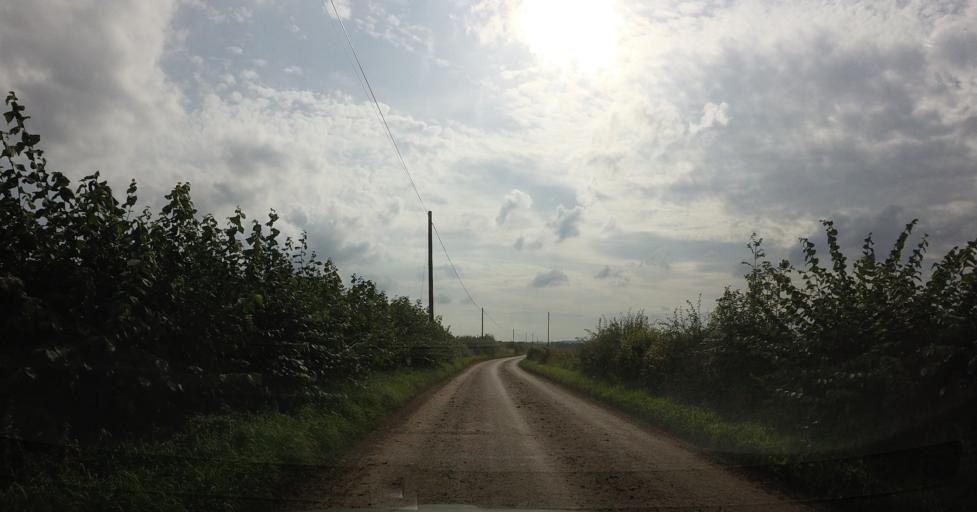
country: GB
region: Scotland
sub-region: Perth and Kinross
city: Auchterarder
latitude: 56.3585
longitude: -3.7071
